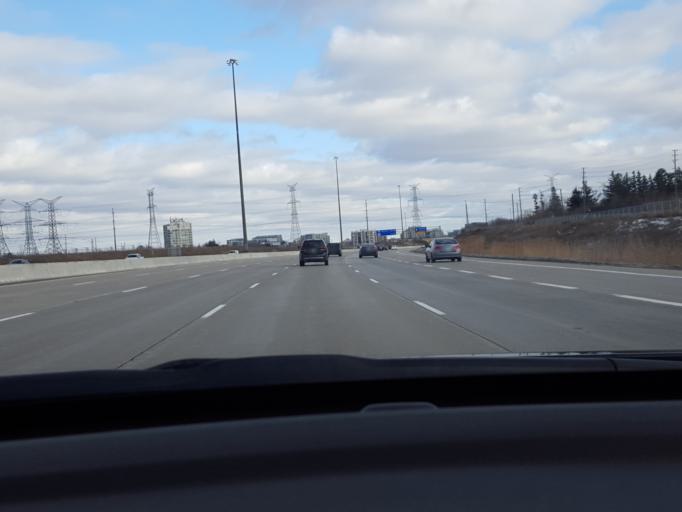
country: CA
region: Ontario
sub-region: York
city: Richmond Hill
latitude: 43.8382
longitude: -79.4169
